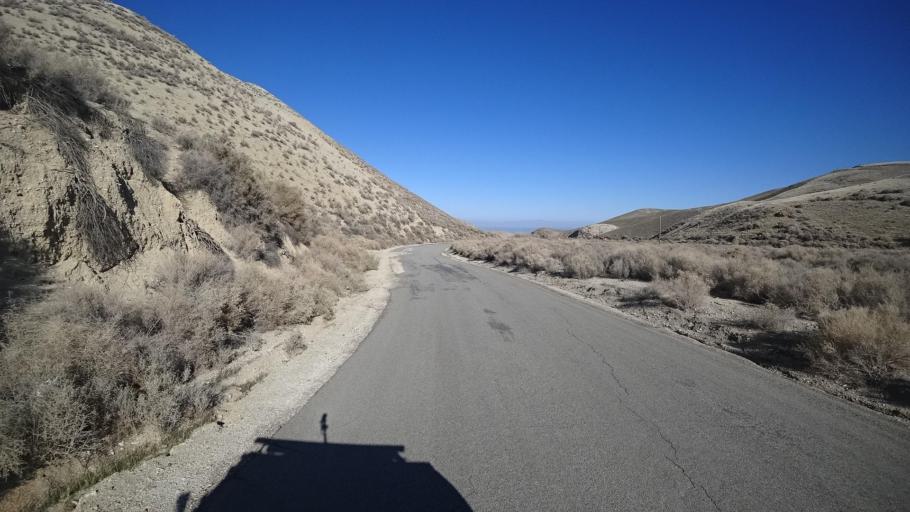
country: US
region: California
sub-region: Kern County
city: Maricopa
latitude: 34.9778
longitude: -119.4064
